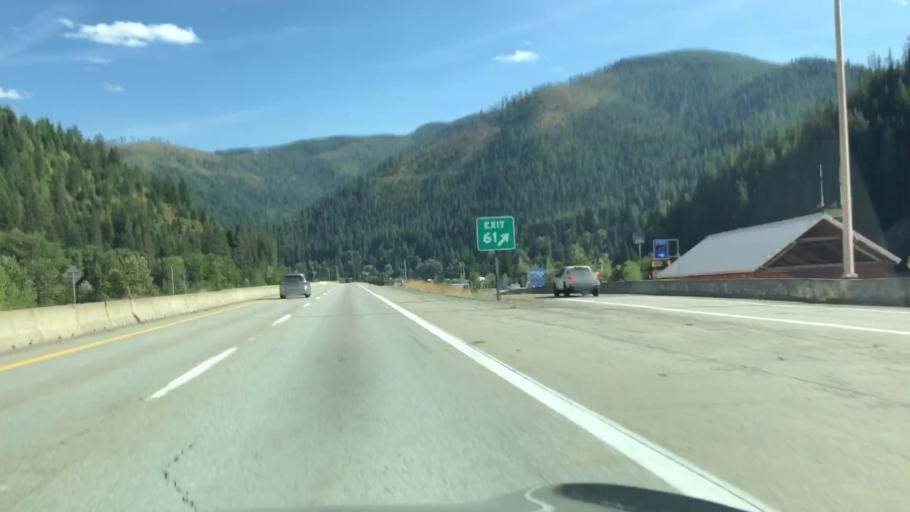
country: US
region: Idaho
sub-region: Shoshone County
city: Wallace
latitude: 47.4795
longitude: -115.9346
